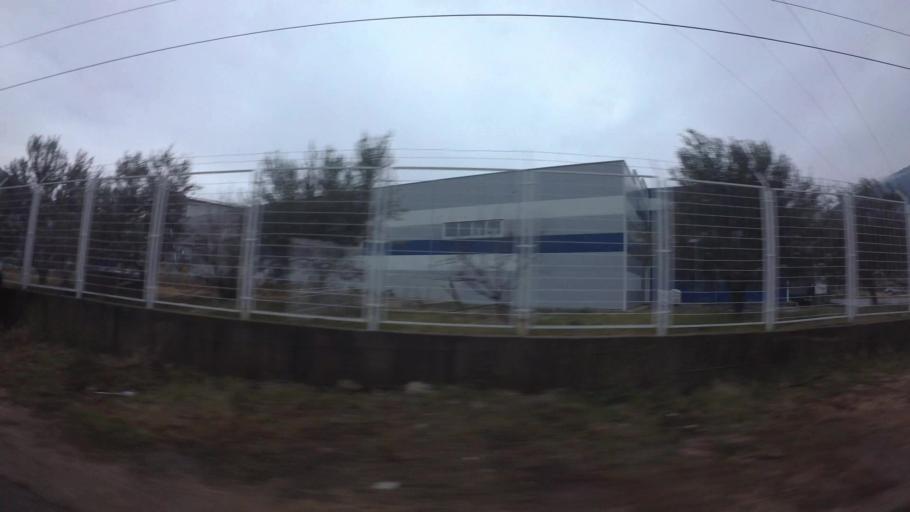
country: BA
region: Federation of Bosnia and Herzegovina
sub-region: Hercegovacko-Bosanski Kanton
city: Mostar
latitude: 43.3684
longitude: 17.8112
